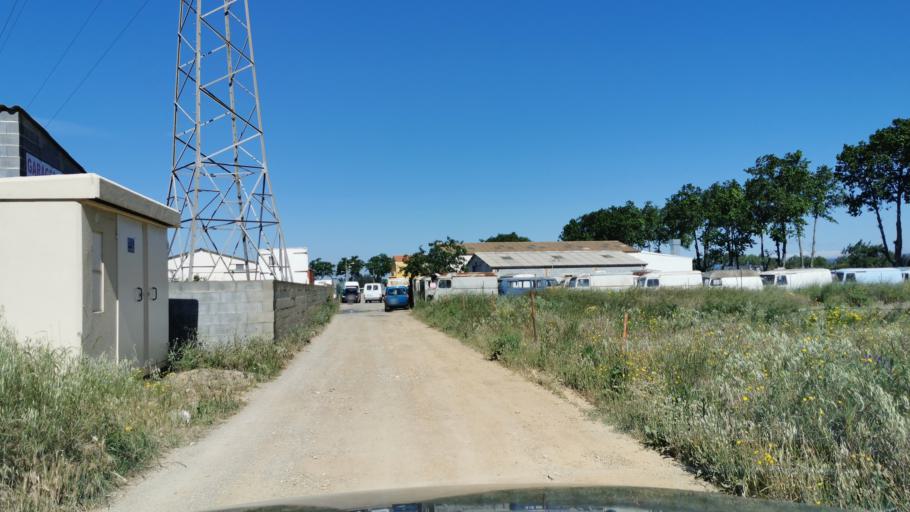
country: FR
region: Languedoc-Roussillon
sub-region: Departement de l'Aude
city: Canet
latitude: 43.2177
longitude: 2.8493
